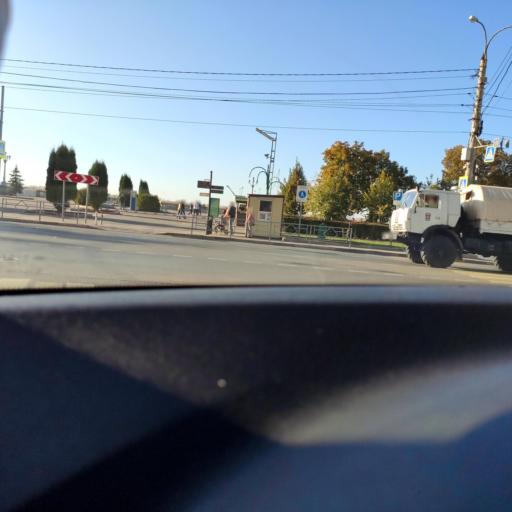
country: RU
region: Samara
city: Rozhdestveno
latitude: 53.1915
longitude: 50.0860
